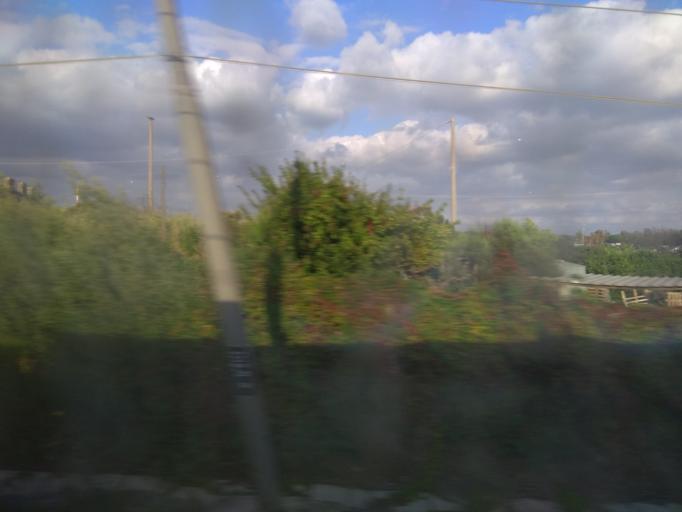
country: IT
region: Latium
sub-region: Citta metropolitana di Roma Capitale
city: Maccarese
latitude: 41.8728
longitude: 12.2436
